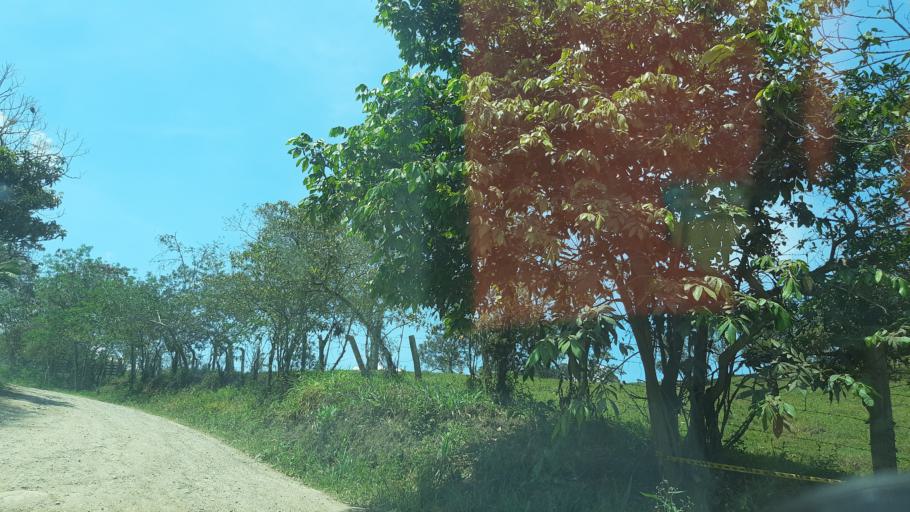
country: CO
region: Boyaca
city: Chinavita
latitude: 5.1320
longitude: -73.3674
